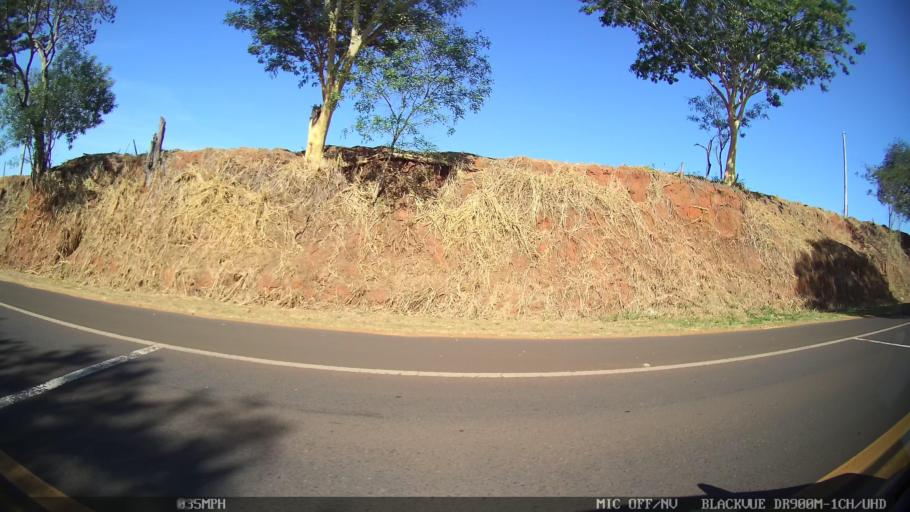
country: BR
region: Sao Paulo
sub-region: Olimpia
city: Olimpia
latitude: -20.7283
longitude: -48.8670
